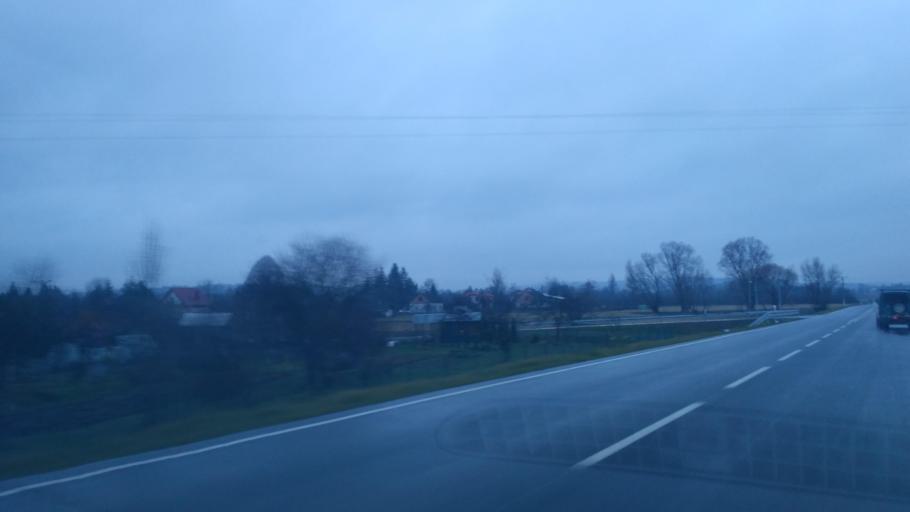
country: PL
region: Subcarpathian Voivodeship
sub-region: Powiat rzeszowski
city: Dynow
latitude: 49.8225
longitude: 22.2411
